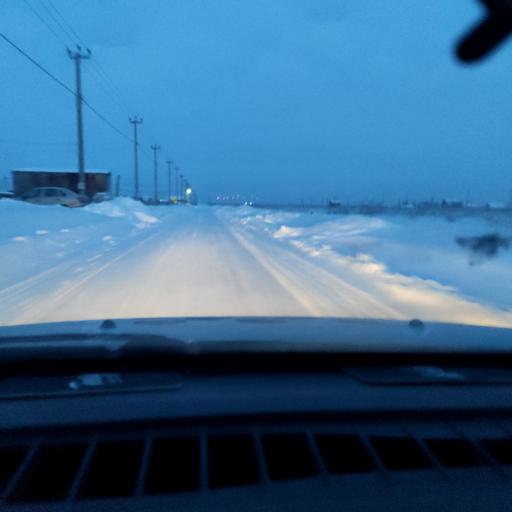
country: RU
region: Perm
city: Kultayevo
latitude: 57.8744
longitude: 55.9759
